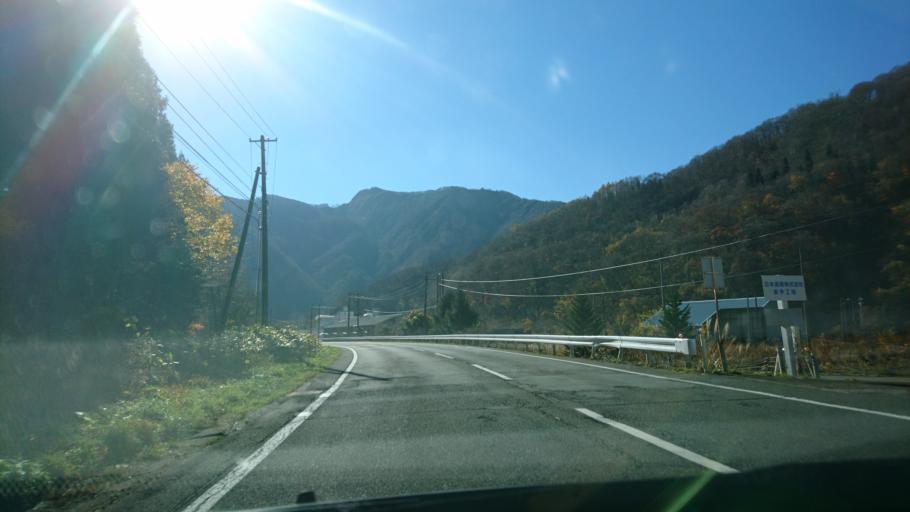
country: JP
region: Iwate
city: Kitakami
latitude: 39.3073
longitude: 140.9021
